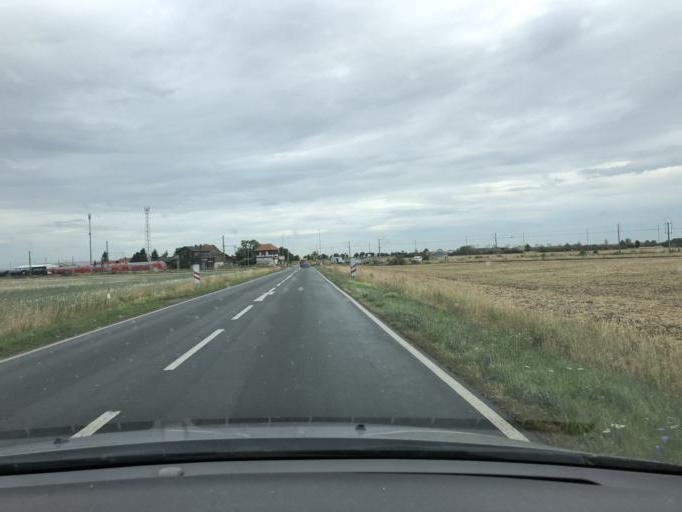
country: DE
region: Saxony-Anhalt
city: Gross Rosenburg
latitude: 51.8687
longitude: 11.8643
